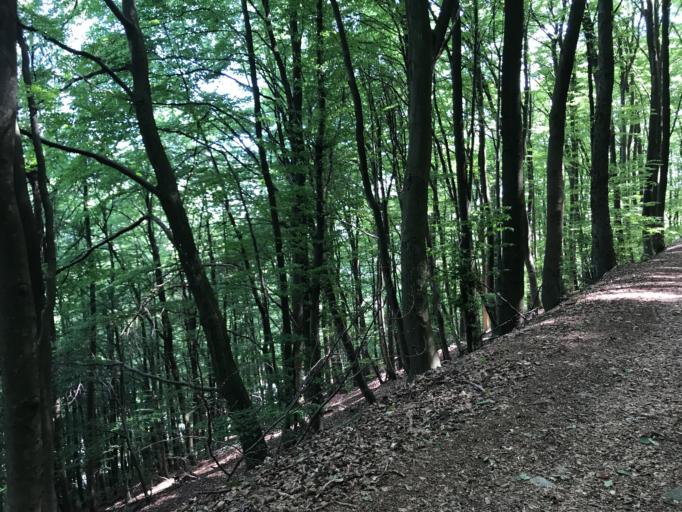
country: DE
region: Hesse
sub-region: Regierungsbezirk Darmstadt
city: Schlangenbad
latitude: 50.0964
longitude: 8.1021
